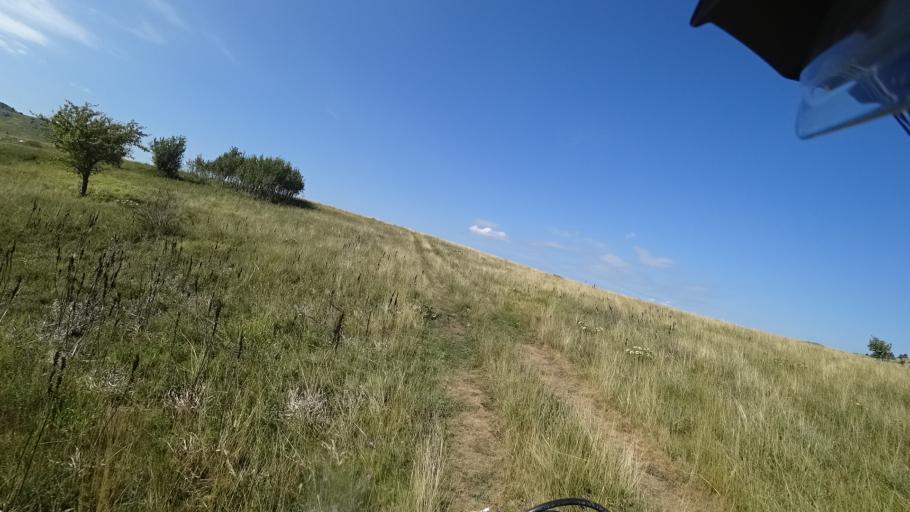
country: HR
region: Zadarska
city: Gracac
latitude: 44.3095
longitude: 15.9778
